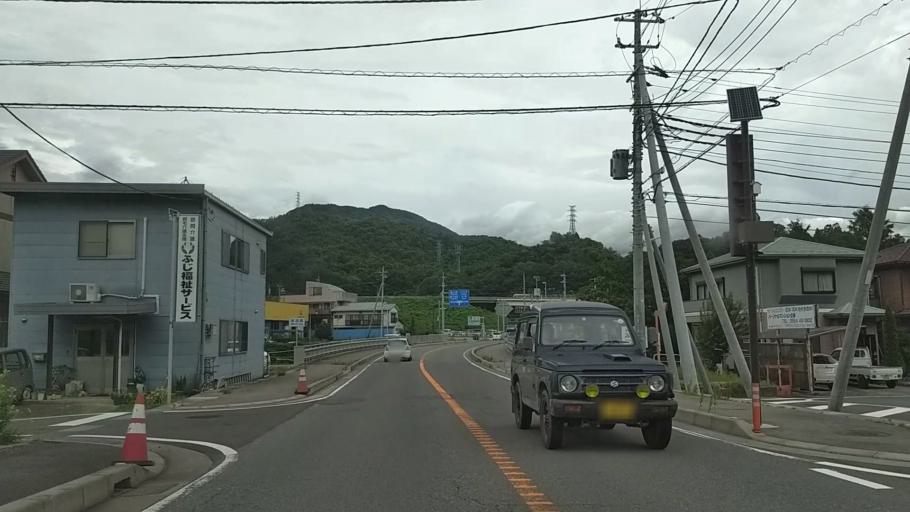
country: JP
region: Yamanashi
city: Otsuki
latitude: 35.5756
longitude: 138.9333
